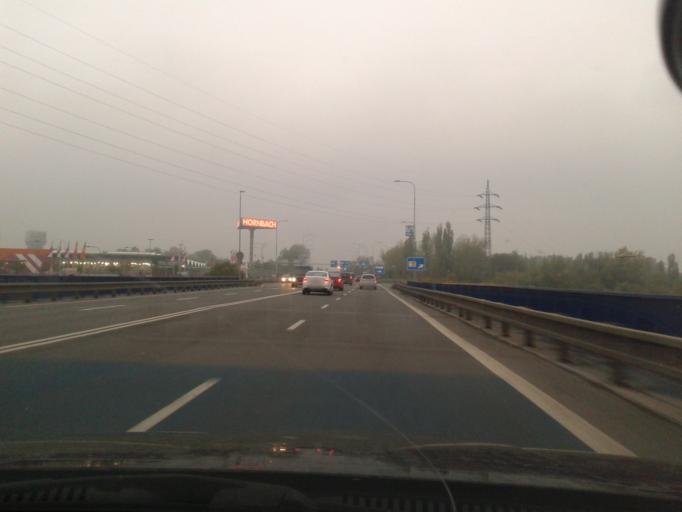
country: CZ
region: Moravskoslezsky
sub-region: Okres Ostrava-Mesto
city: Ostrava
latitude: 49.8059
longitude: 18.2819
